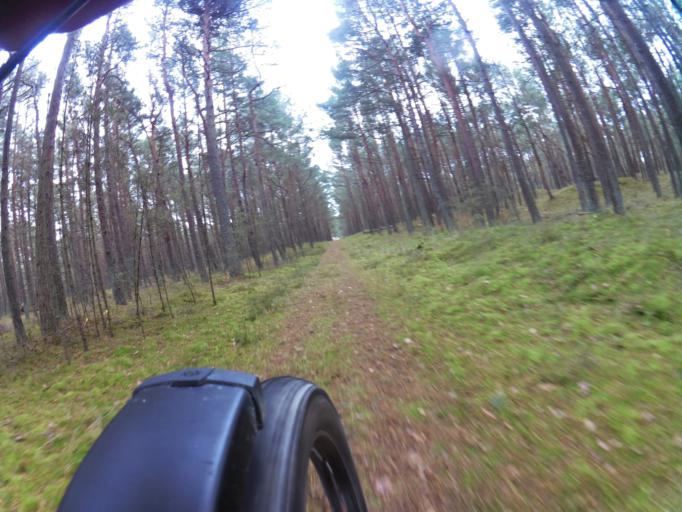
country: PL
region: Pomeranian Voivodeship
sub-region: Powiat leborski
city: Leba
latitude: 54.7697
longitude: 17.5976
